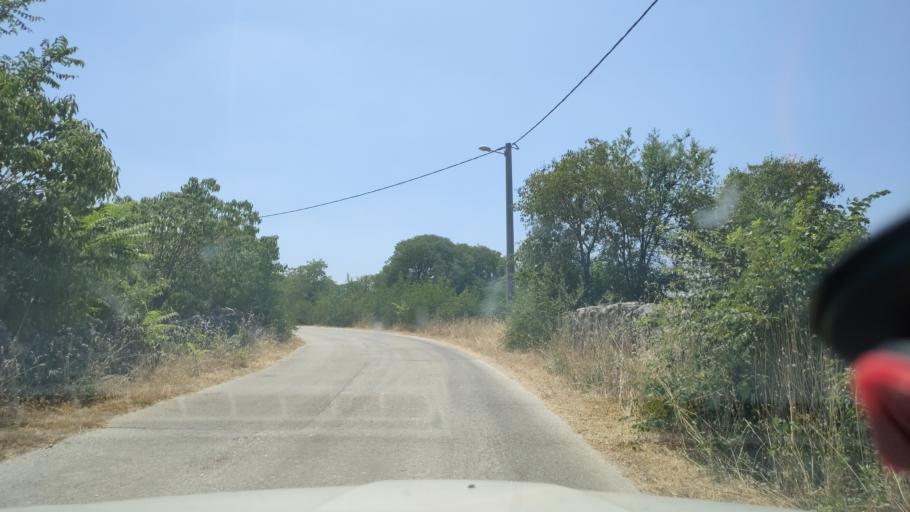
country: HR
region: Sibensko-Kniniska
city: Kistanje
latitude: 43.9519
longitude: 15.8820
